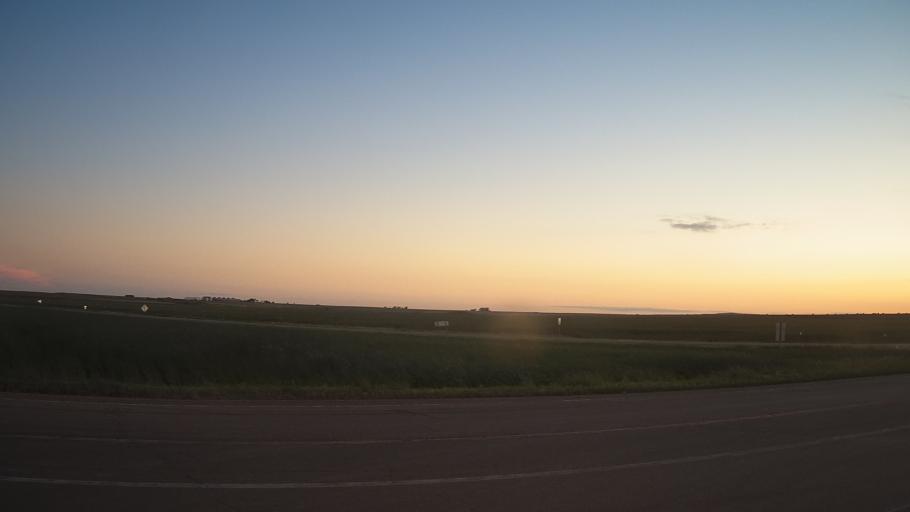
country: US
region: South Dakota
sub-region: Buffalo County
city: Fort Thompson
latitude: 43.8752
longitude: -99.6050
